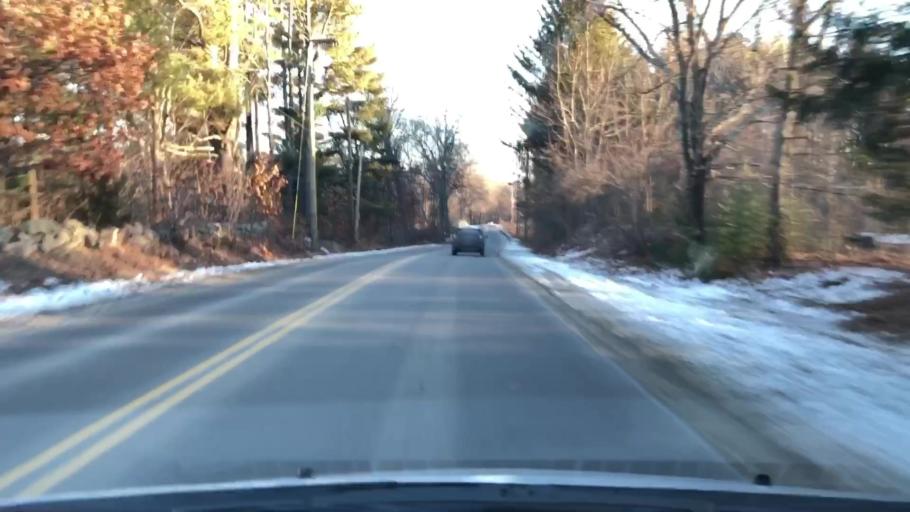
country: US
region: New Hampshire
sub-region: Hillsborough County
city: Milford
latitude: 42.8285
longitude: -71.5867
